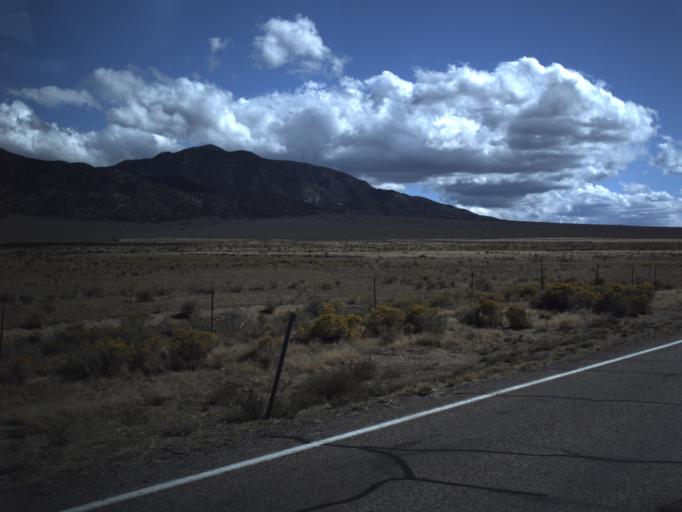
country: US
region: Utah
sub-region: Beaver County
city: Milford
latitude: 38.3308
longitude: -112.9732
